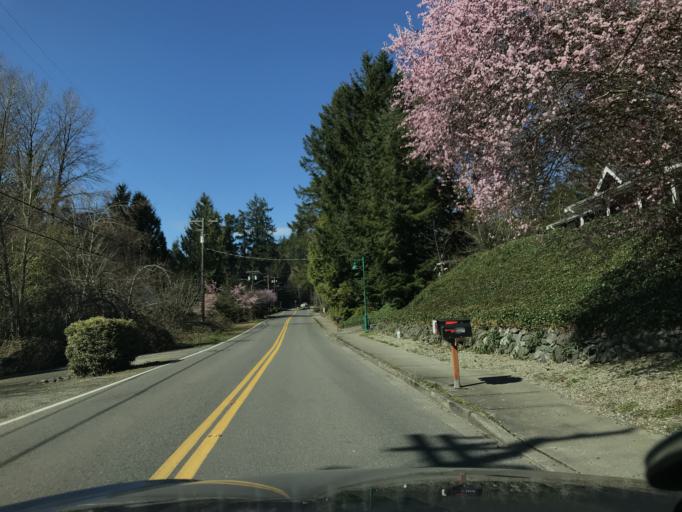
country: US
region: Washington
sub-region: Pierce County
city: Gig Harbor
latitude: 47.3404
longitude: -122.5949
